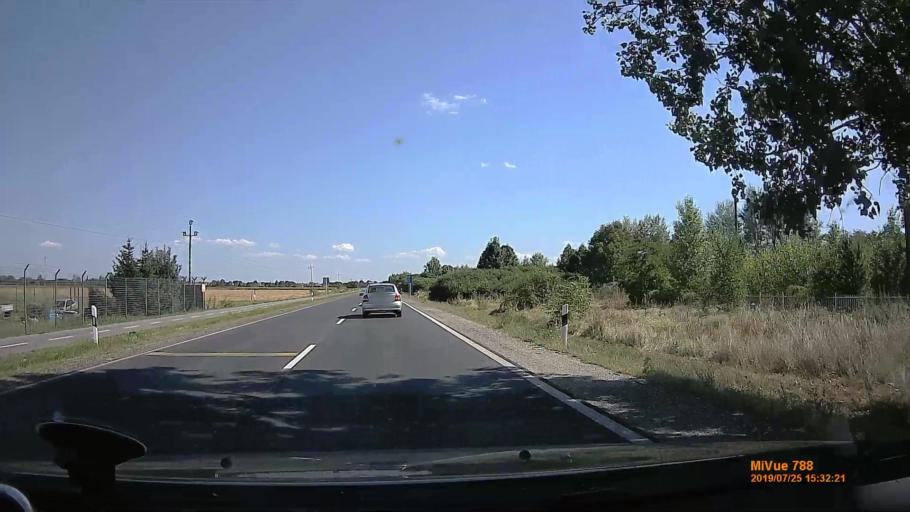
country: HU
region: Borsod-Abauj-Zemplen
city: Malyi
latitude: 48.0072
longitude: 20.8279
